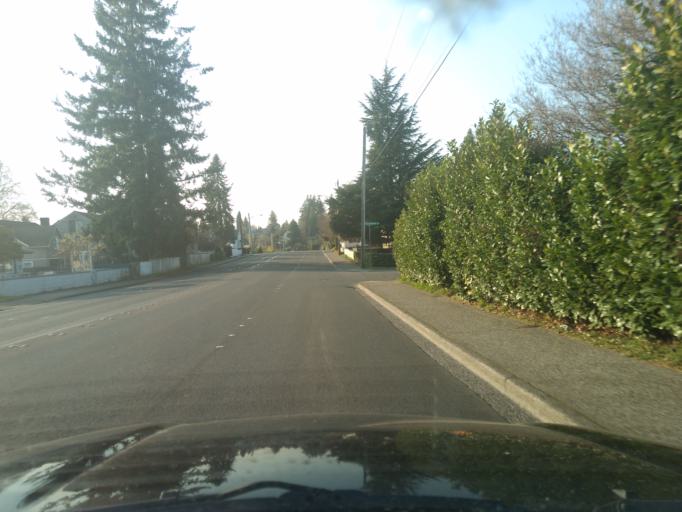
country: US
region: Washington
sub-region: Kitsap County
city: Bremerton
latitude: 47.5711
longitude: -122.6496
